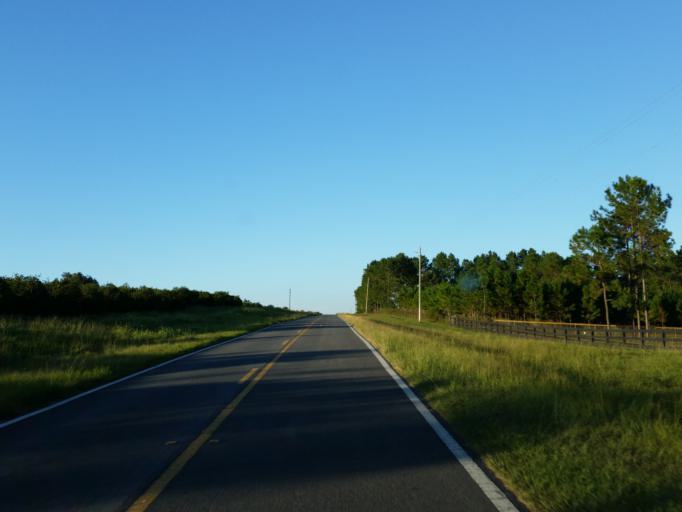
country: US
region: Florida
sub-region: Hernando County
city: Hill 'n Dale
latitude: 28.4423
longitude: -82.2698
